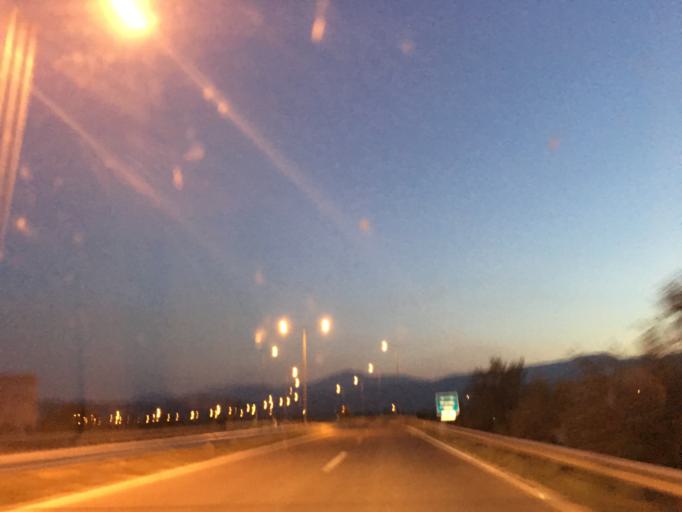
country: MK
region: Petrovec
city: Petrovec
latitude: 41.9406
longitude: 21.6278
